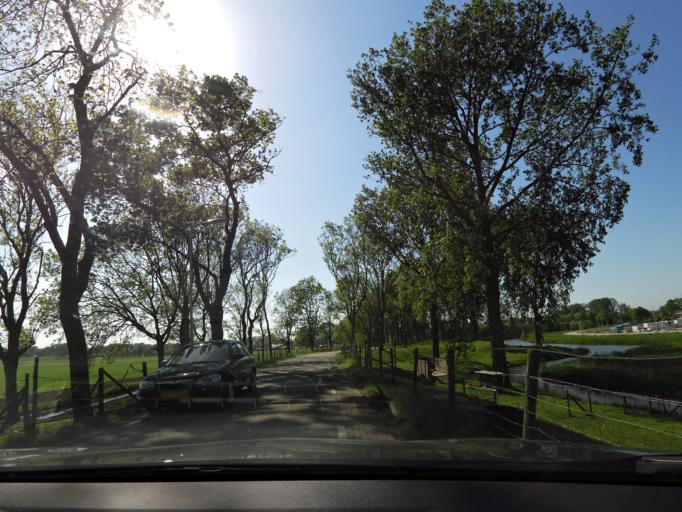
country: NL
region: South Holland
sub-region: Gemeente Albrandswaard
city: Rhoon
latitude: 51.8509
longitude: 4.4321
